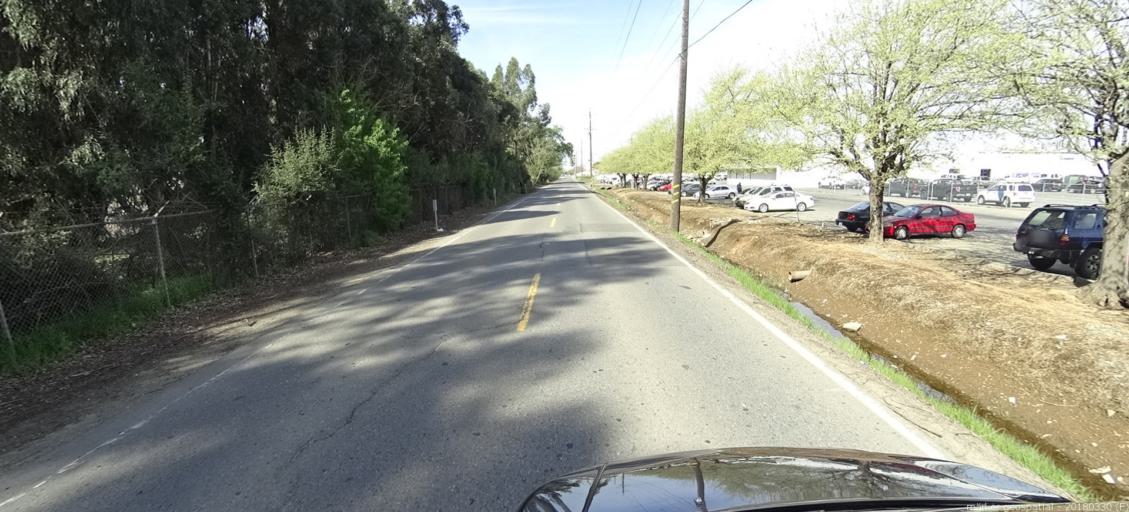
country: US
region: California
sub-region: Sacramento County
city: Rosemont
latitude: 38.5471
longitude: -121.3826
